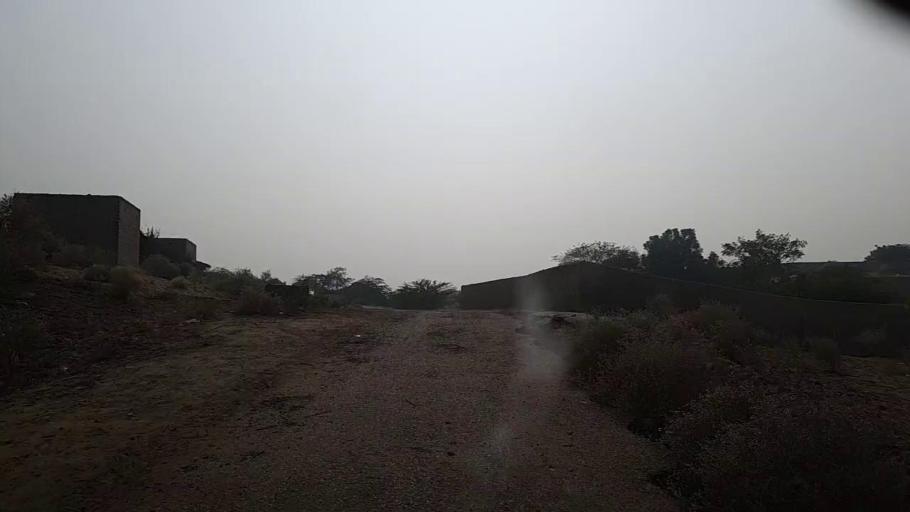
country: PK
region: Sindh
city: Bozdar
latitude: 27.0682
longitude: 68.6322
